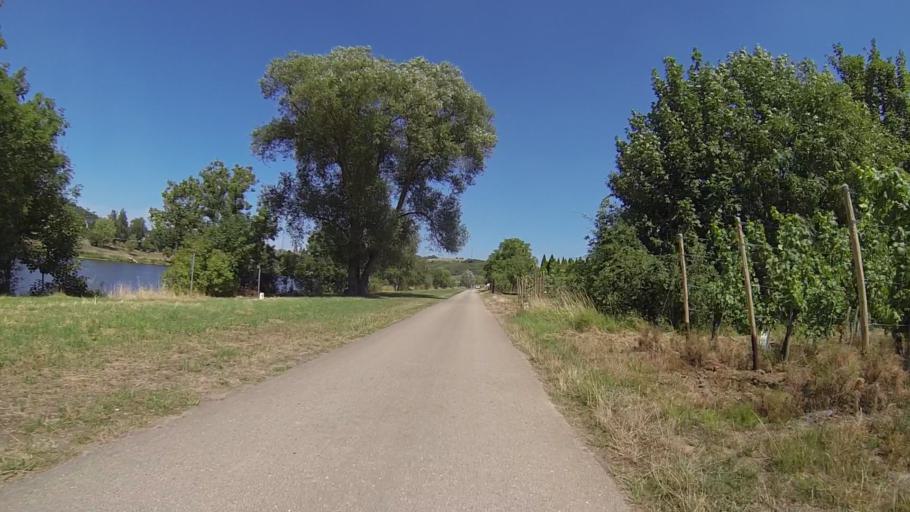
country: LU
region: Grevenmacher
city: Wasserbillig
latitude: 49.7096
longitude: 6.4978
